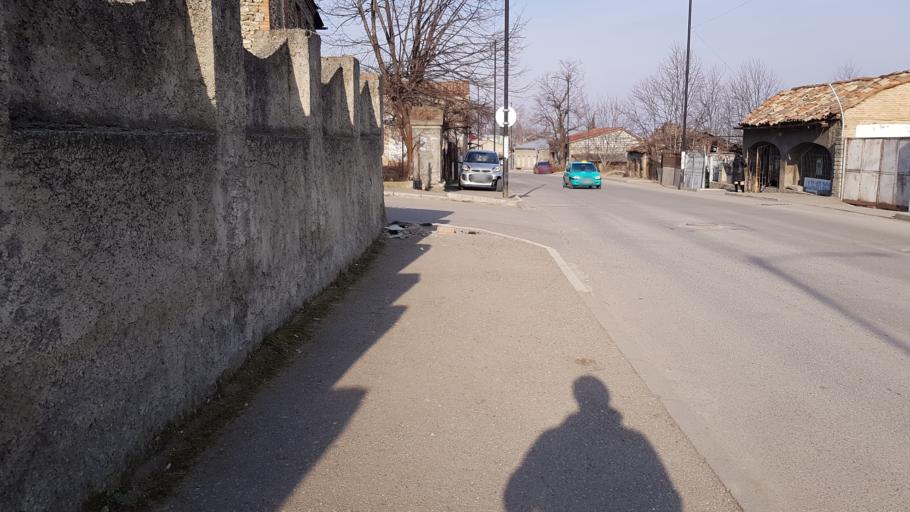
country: GE
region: Kakheti
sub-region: Telavi
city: Telavi
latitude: 41.9245
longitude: 45.4585
